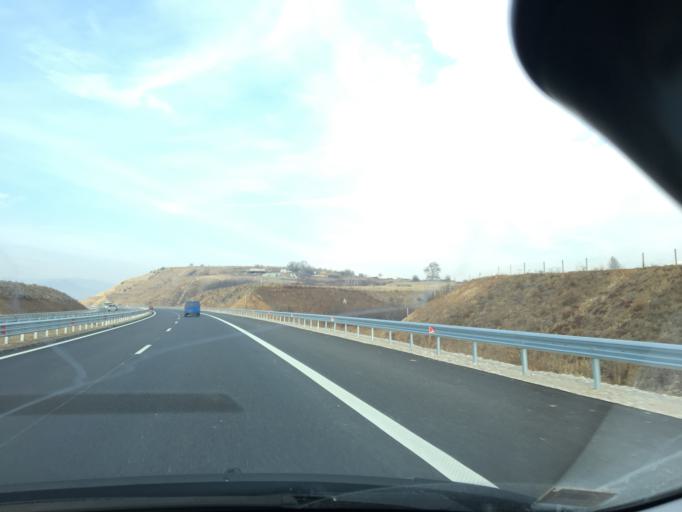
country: BG
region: Blagoevgrad
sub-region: Obshtina Sandanski
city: Sandanski
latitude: 41.5237
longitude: 23.2696
